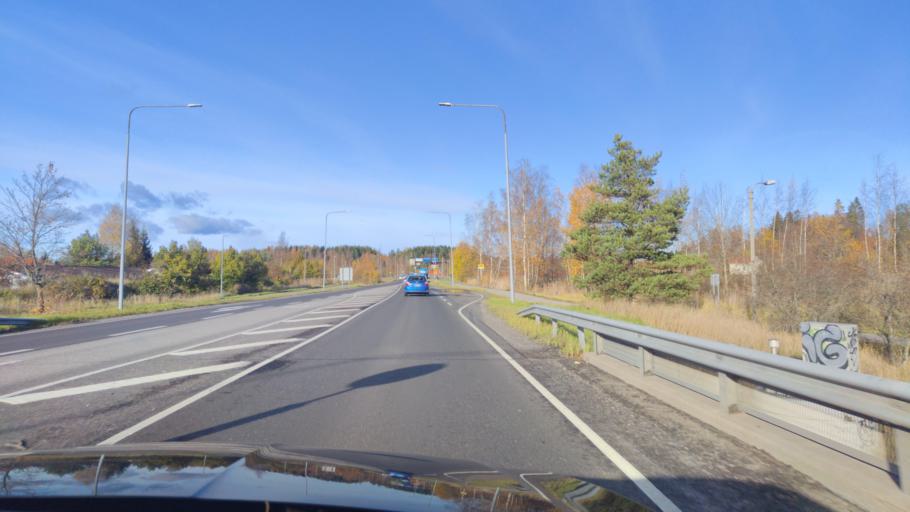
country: FI
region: Varsinais-Suomi
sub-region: Turku
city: Kaarina
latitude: 60.4335
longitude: 22.3845
